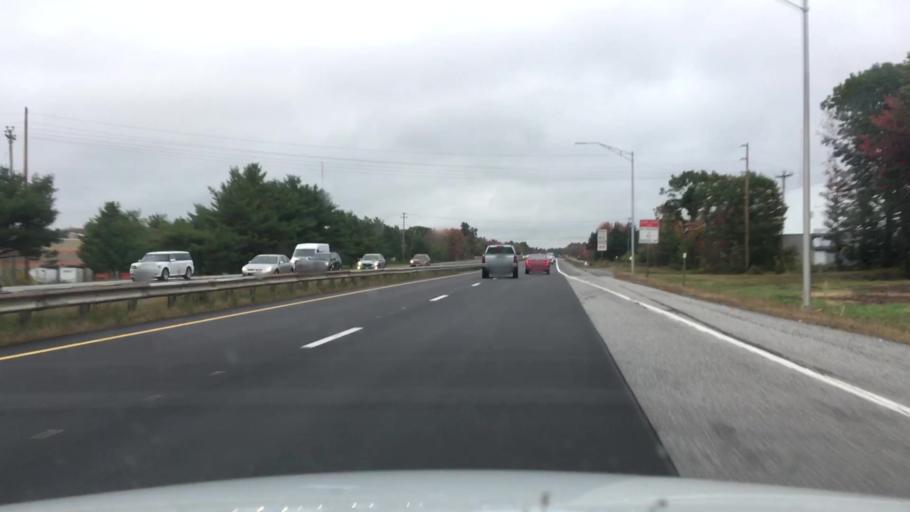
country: US
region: Maine
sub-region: Cumberland County
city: South Portland Gardens
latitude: 43.6838
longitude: -70.3236
